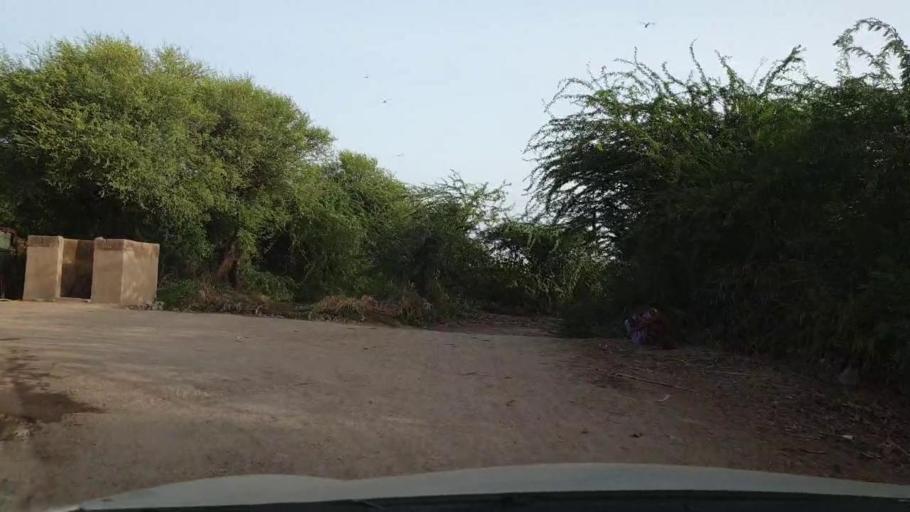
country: PK
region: Sindh
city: Tando Ghulam Ali
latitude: 25.0983
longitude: 68.8848
